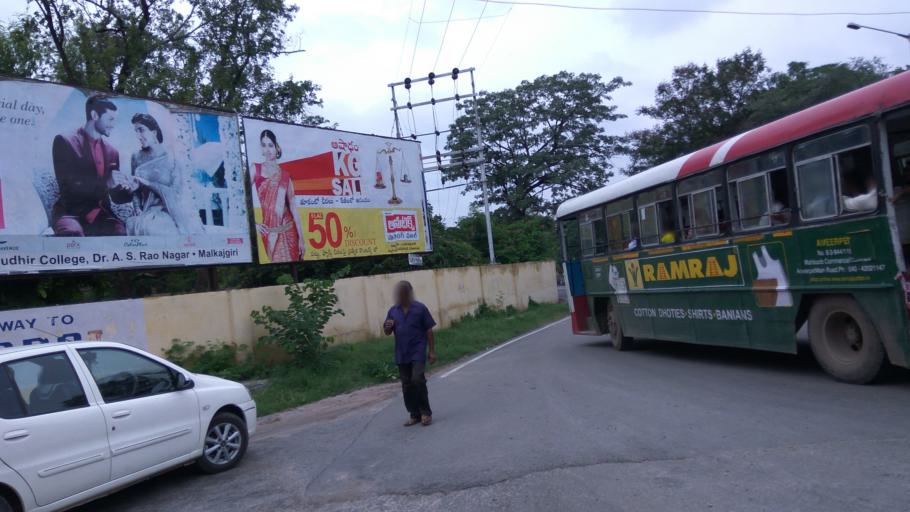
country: IN
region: Telangana
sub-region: Hyderabad
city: Malkajgiri
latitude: 17.4357
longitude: 78.5227
